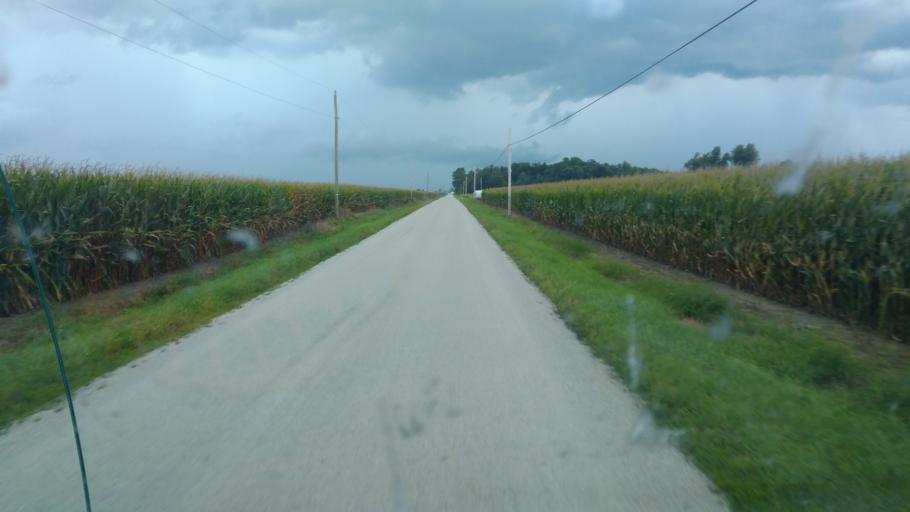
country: US
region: Ohio
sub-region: Hardin County
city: Kenton
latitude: 40.6590
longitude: -83.5148
